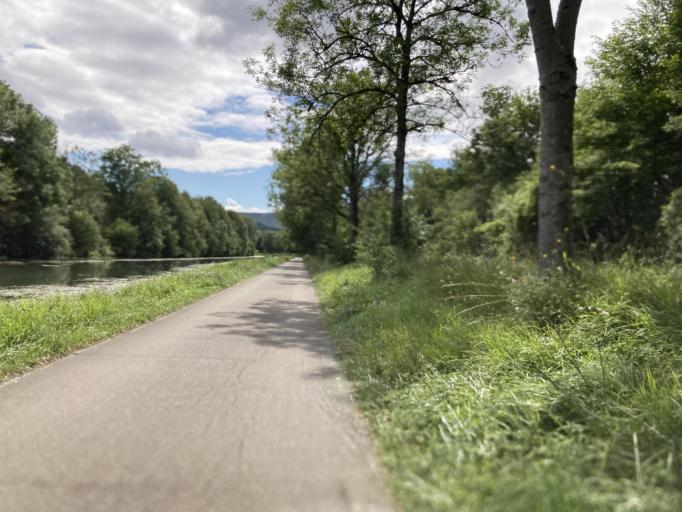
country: FR
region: Bourgogne
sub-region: Departement de la Cote-d'Or
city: Plombieres-les-Dijon
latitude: 47.3282
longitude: 4.9368
